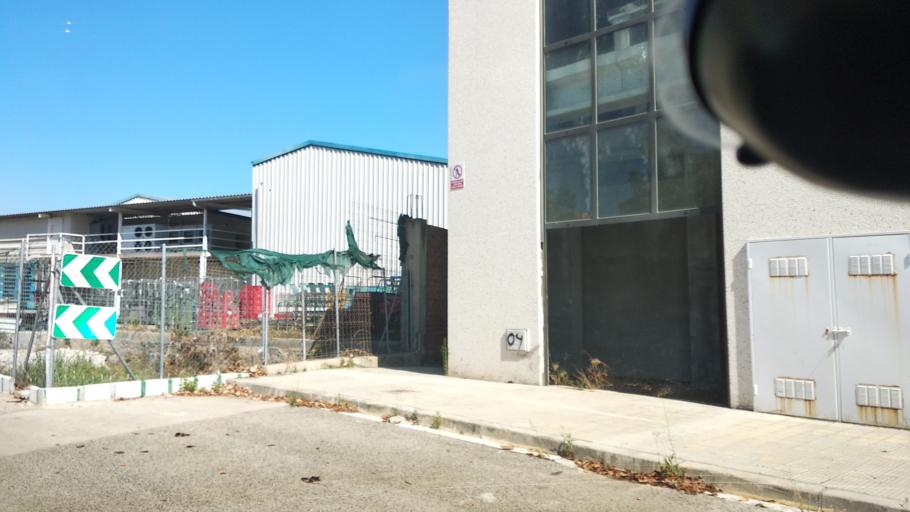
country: ES
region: Catalonia
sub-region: Provincia de Tarragona
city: El Vendrell
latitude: 41.2111
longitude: 1.5329
